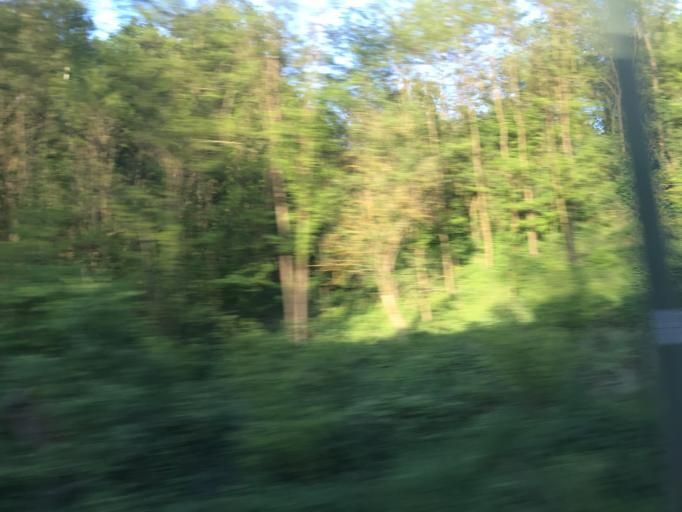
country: DE
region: Rheinland-Pfalz
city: Dudenhofen
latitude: 49.3520
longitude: 8.3999
